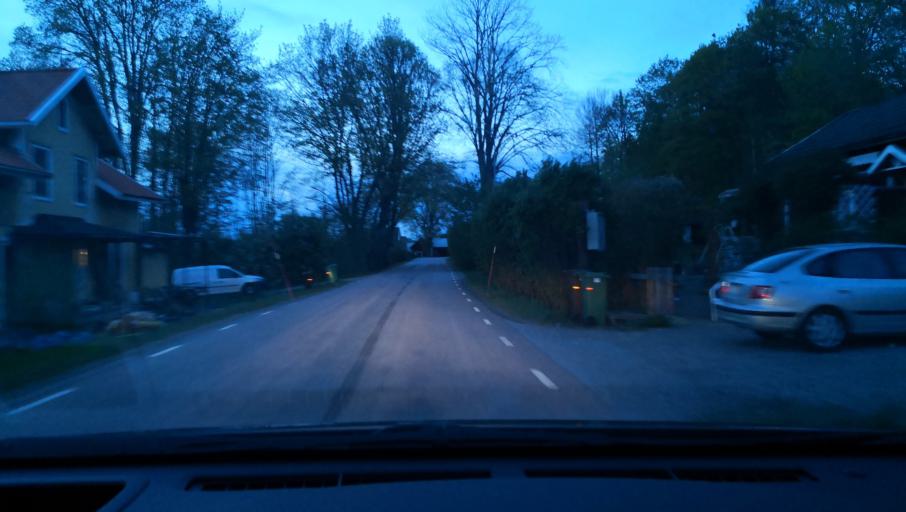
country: SE
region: OErebro
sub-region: Askersunds Kommun
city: Asbro
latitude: 59.0715
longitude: 15.0042
